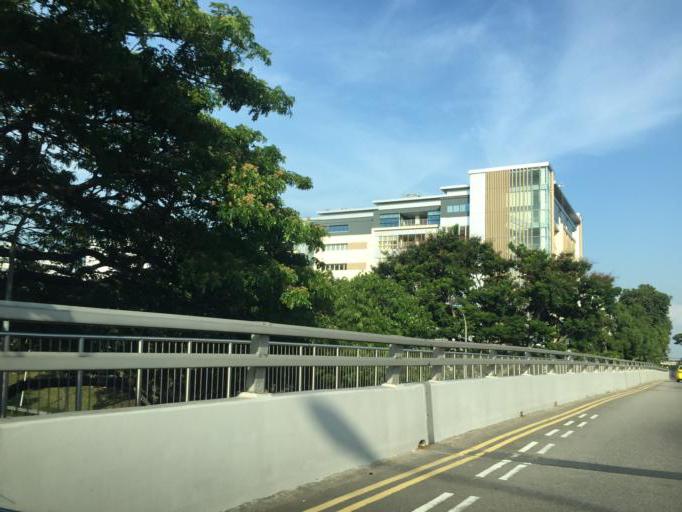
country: SG
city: Singapore
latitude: 1.3419
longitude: 103.9468
